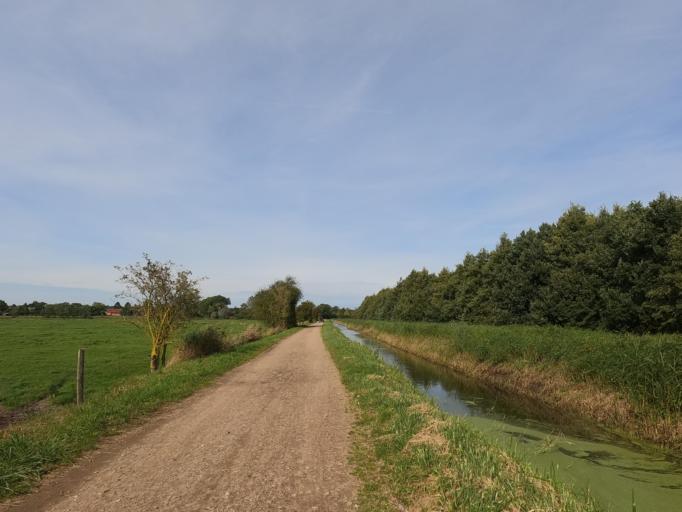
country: DE
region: Schleswig-Holstein
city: Gromitz
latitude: 54.1645
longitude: 10.9930
